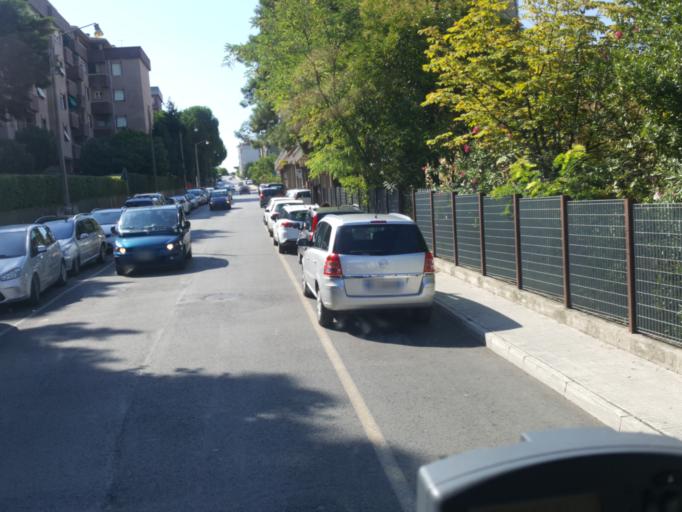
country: IT
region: The Marches
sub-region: Provincia di Ancona
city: Le Grazie di Ancona
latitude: 43.5976
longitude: 13.5181
